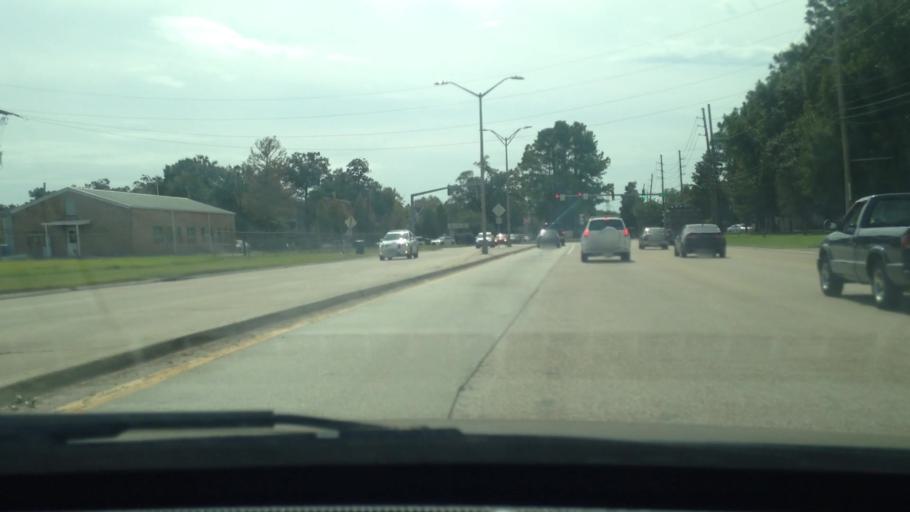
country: US
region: Louisiana
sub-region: Jefferson Parish
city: River Ridge
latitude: 29.9697
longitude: -90.2047
